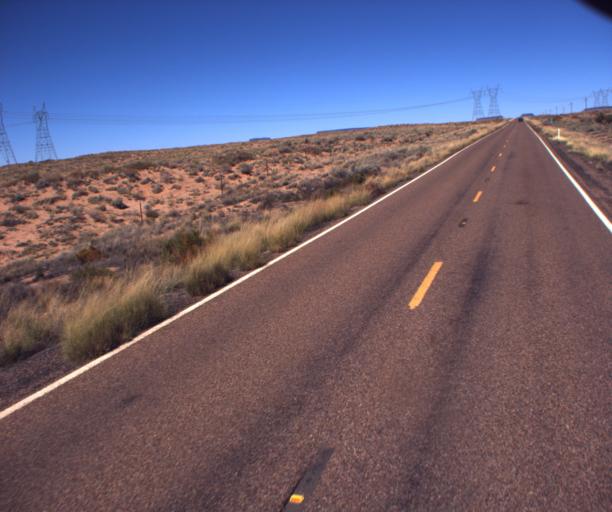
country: US
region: Arizona
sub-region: Navajo County
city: Holbrook
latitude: 35.1560
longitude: -110.0838
